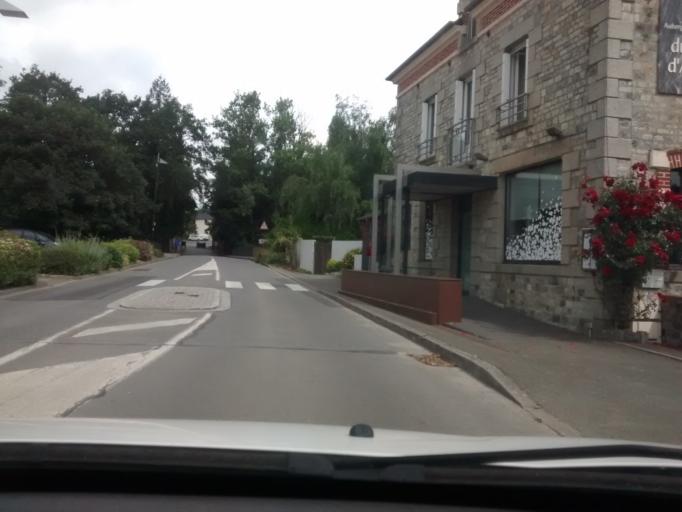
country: FR
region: Brittany
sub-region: Departement d'Ille-et-Vilaine
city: Acigne
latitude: 48.1304
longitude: -1.5346
